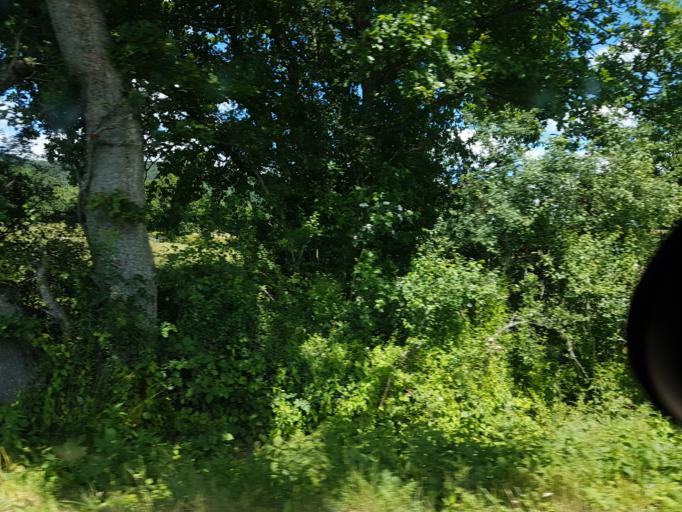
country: FR
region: Bourgogne
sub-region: Departement de Saone-et-Loire
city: Curgy
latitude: 47.0547
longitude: 4.3234
